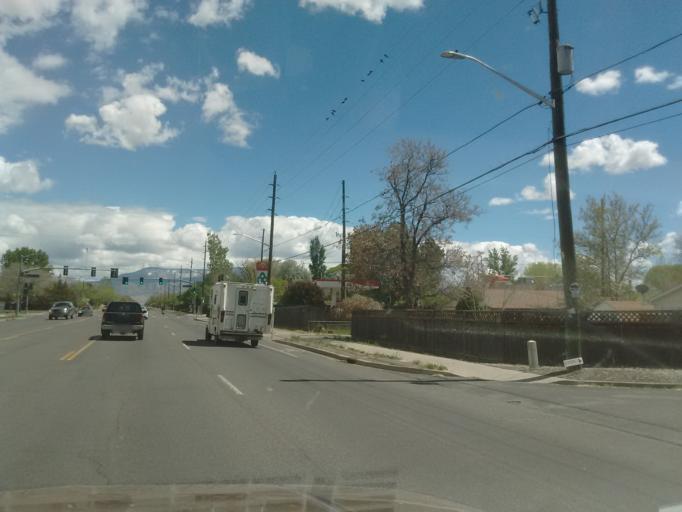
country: US
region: Colorado
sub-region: Mesa County
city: Fruitvale
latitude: 39.0918
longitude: -108.5070
